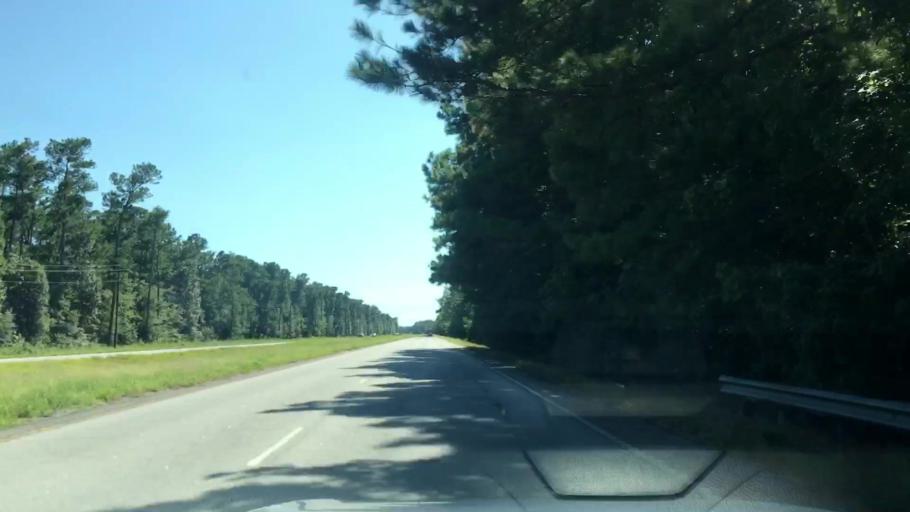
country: US
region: South Carolina
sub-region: Charleston County
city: Awendaw
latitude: 33.0678
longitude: -79.5263
